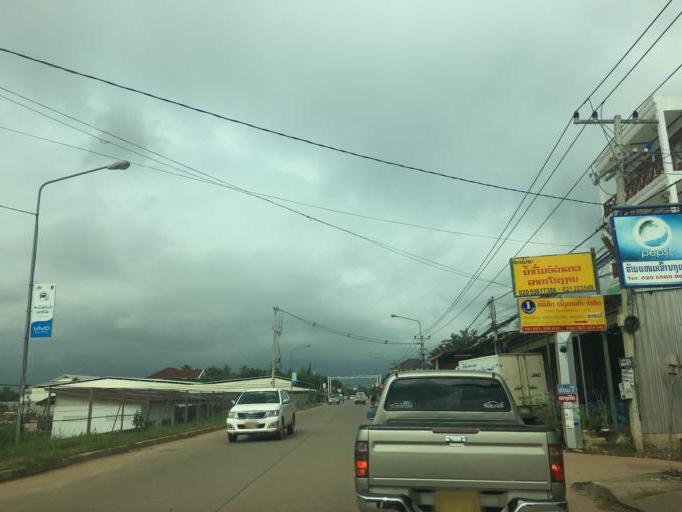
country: TH
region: Nong Khai
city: Si Chiang Mai
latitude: 17.9746
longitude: 102.5499
